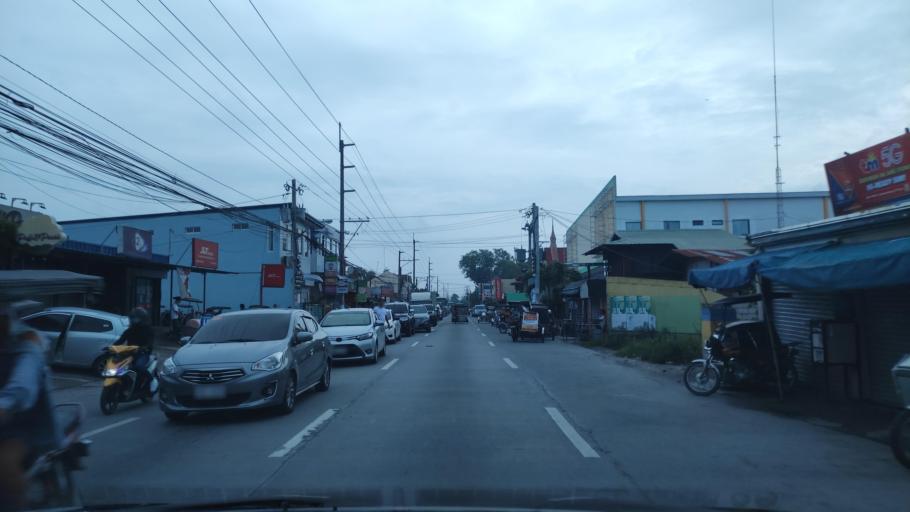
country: PH
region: Central Luzon
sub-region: Province of Pampanga
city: Santa Ana
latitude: 15.0961
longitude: 120.7671
